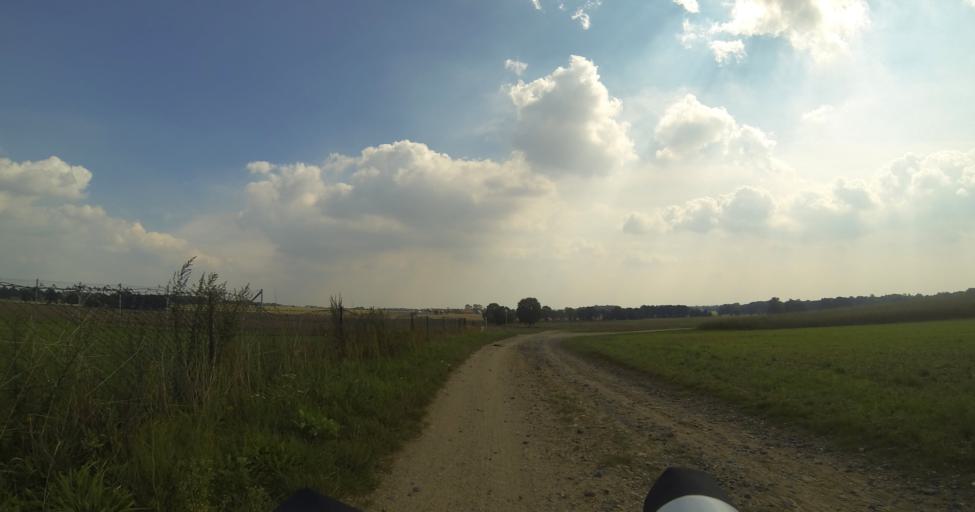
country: DE
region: Saxony
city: Grossenhain
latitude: 51.2637
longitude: 13.5526
